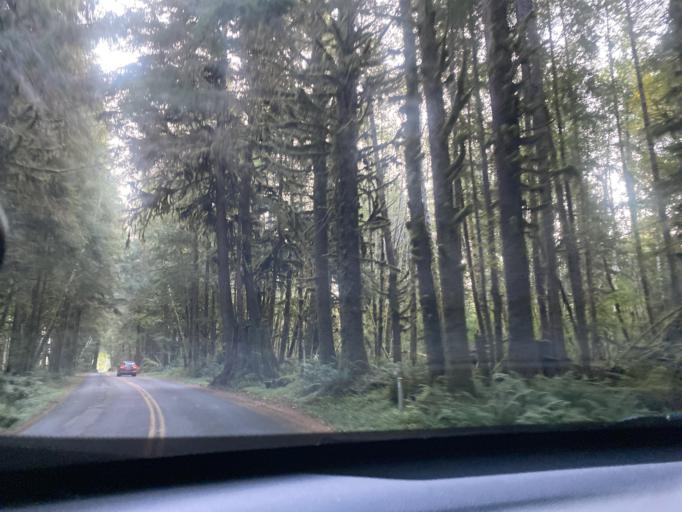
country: US
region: Washington
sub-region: Clallam County
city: Forks
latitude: 47.8168
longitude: -124.0442
